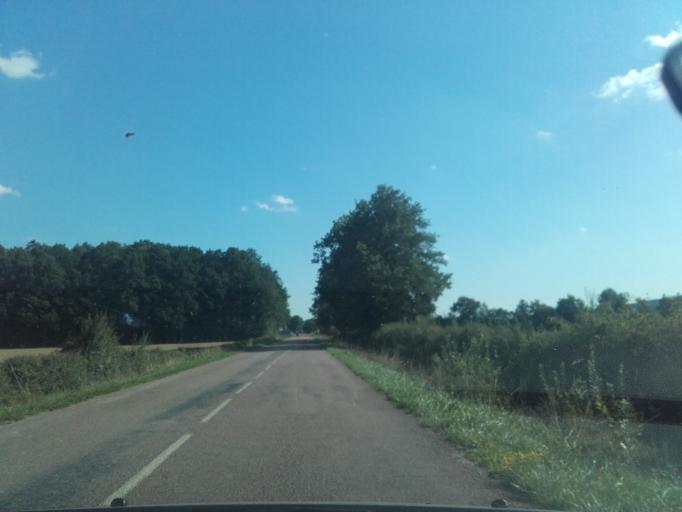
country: FR
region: Bourgogne
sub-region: Departement de Saone-et-Loire
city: Epinac
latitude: 46.9916
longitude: 4.4827
